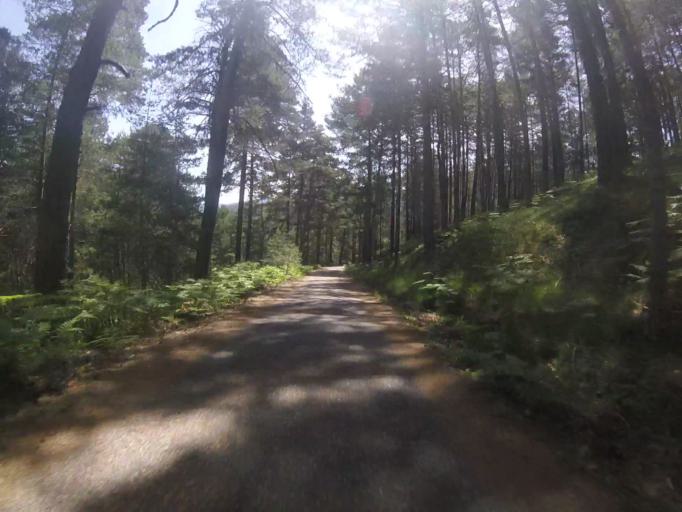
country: ES
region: Madrid
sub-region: Provincia de Madrid
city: Cercedilla
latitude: 40.8082
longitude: -4.0443
